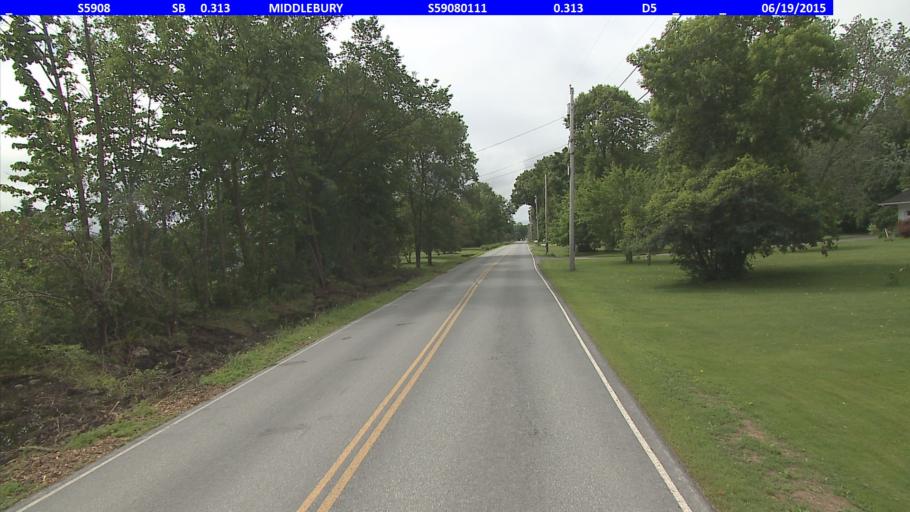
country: US
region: Vermont
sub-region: Addison County
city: Middlebury (village)
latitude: 44.0000
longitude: -73.1345
